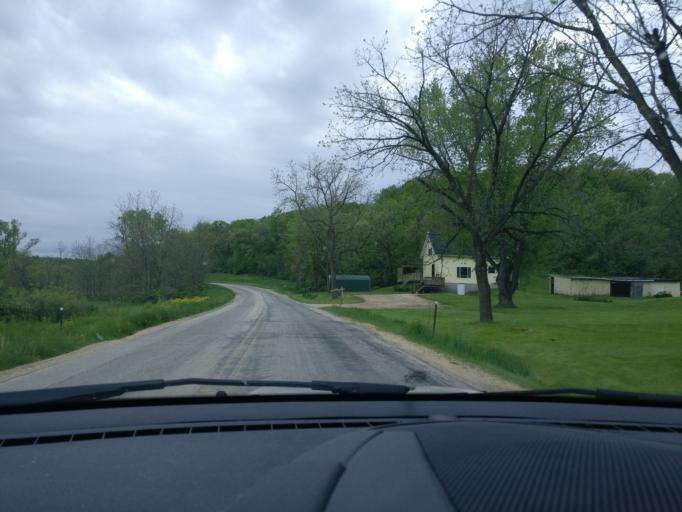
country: US
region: Wisconsin
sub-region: Lafayette County
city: Darlington
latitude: 42.7737
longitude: -90.0013
